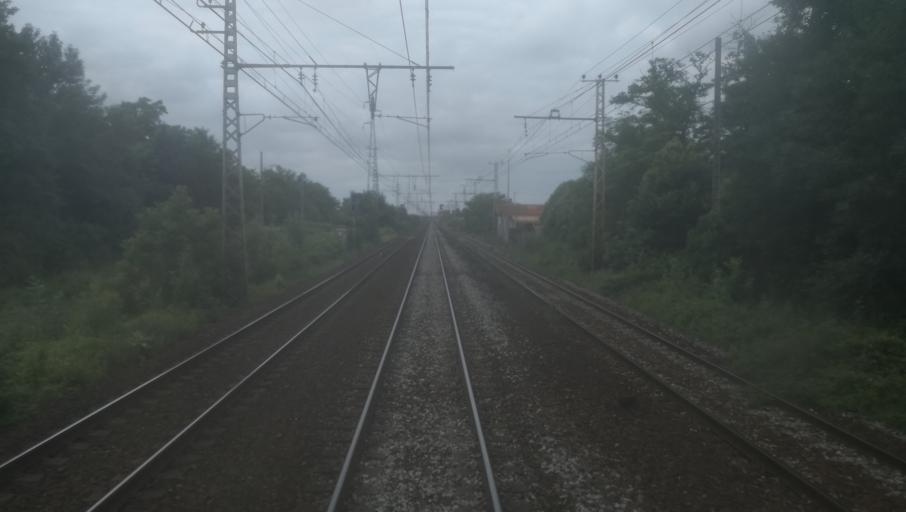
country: FR
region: Midi-Pyrenees
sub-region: Departement de la Haute-Garonne
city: Fenouillet
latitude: 43.6756
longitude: 1.4064
